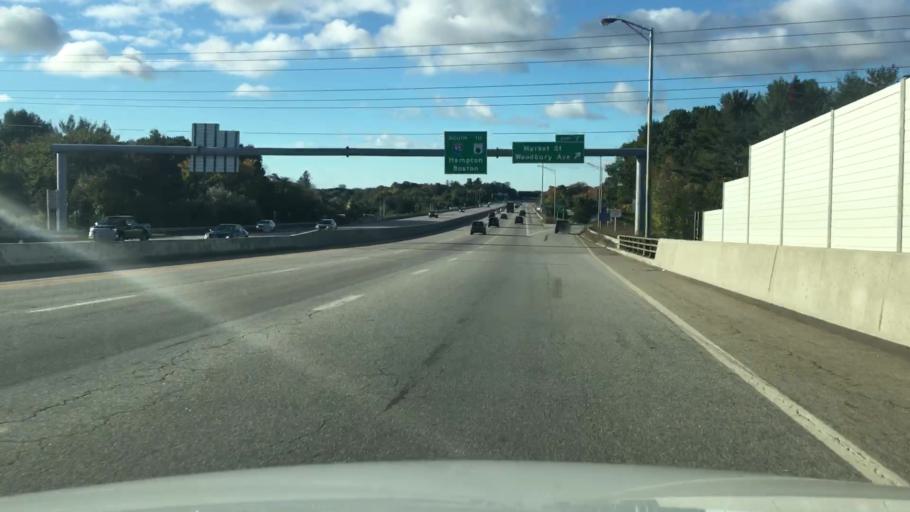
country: US
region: New Hampshire
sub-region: Rockingham County
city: Portsmouth
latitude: 43.0880
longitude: -70.7722
